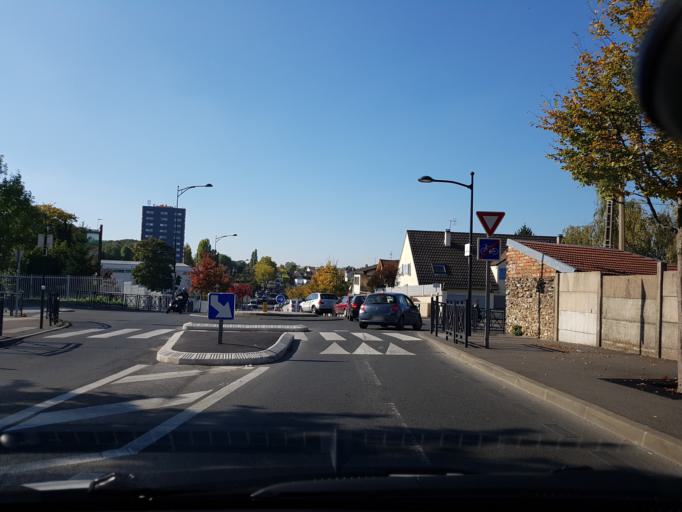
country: FR
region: Ile-de-France
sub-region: Departement du Val-de-Marne
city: Chennevieres-sur-Marne
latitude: 48.8110
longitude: 2.5397
